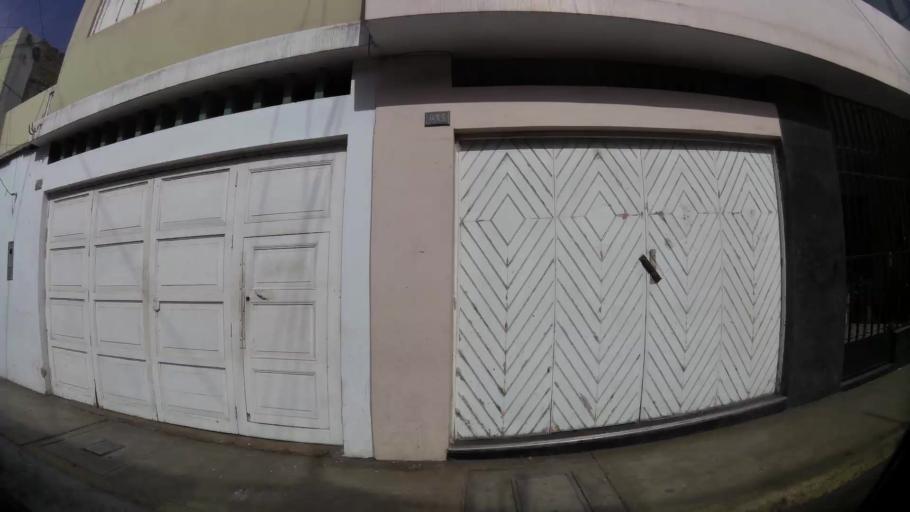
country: PE
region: La Libertad
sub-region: Provincia de Trujillo
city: Trujillo
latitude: -8.1091
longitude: -79.0151
